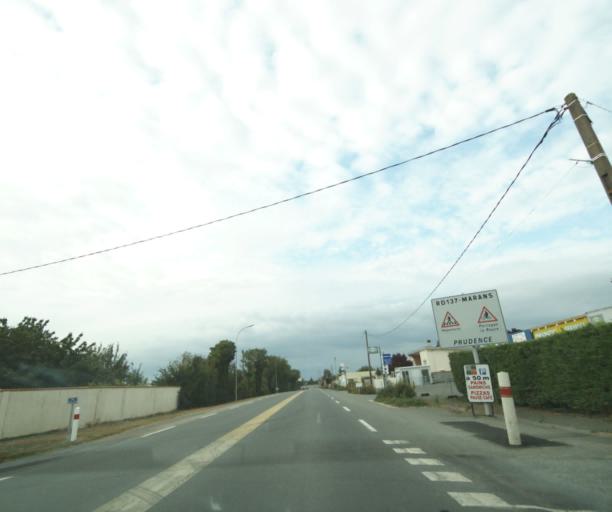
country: FR
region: Poitou-Charentes
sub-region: Departement de la Charente-Maritime
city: Marans
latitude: 46.2988
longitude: -0.9907
